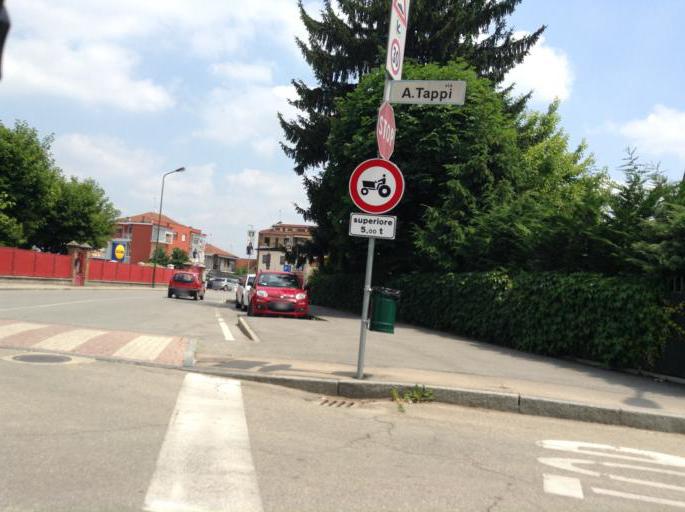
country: IT
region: Piedmont
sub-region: Provincia di Torino
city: Carignano
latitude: 44.9087
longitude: 7.6699
